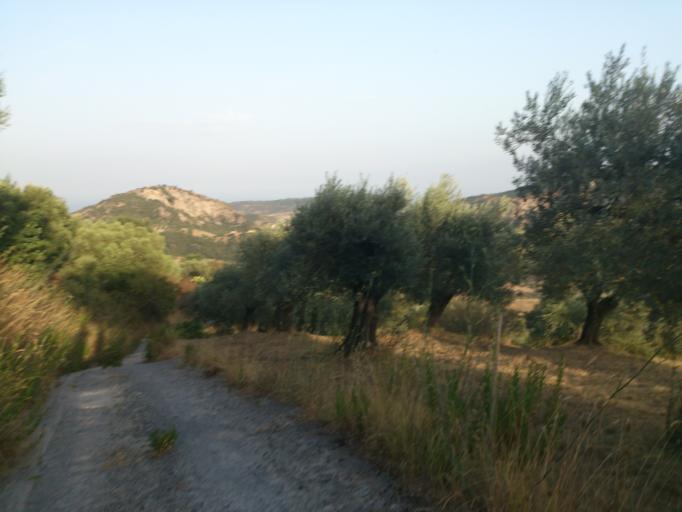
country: IT
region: Calabria
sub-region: Provincia di Reggio Calabria
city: Pazzano
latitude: 38.4489
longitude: 16.4533
